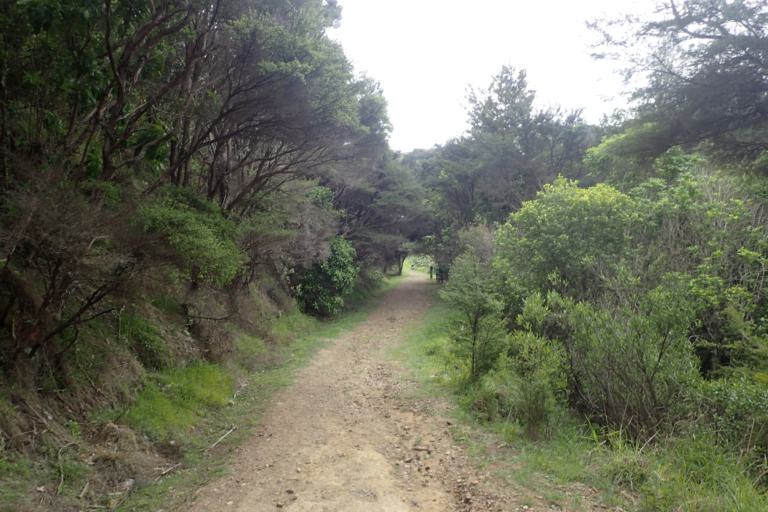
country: NZ
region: Auckland
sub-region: Auckland
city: Pakuranga
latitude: -36.7833
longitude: 174.9967
